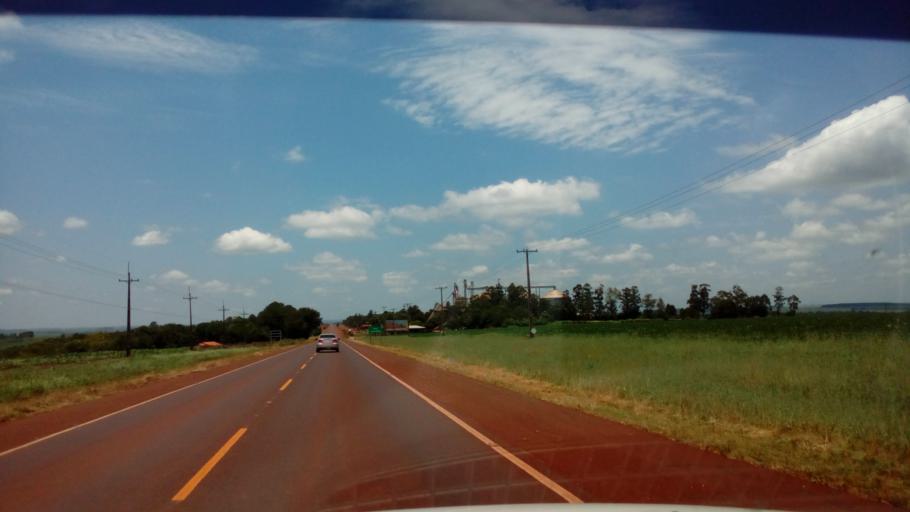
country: PY
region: Alto Parana
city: Naranjal
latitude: -26.0131
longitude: -55.1252
